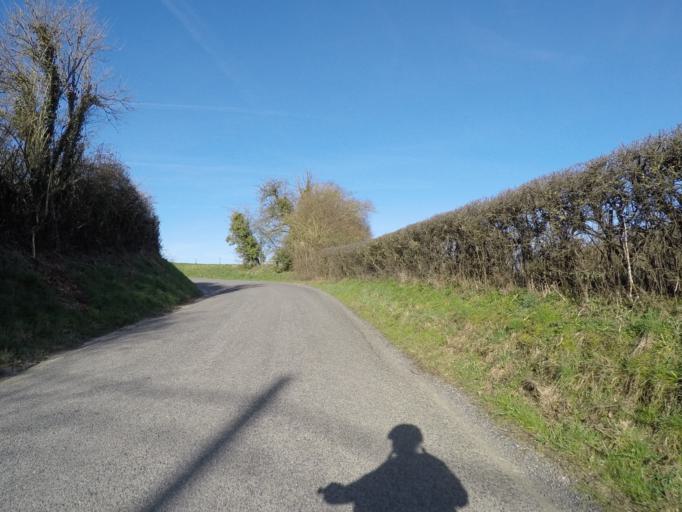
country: BE
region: Wallonia
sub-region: Province de Namur
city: Gesves
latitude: 50.3593
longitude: 5.0857
